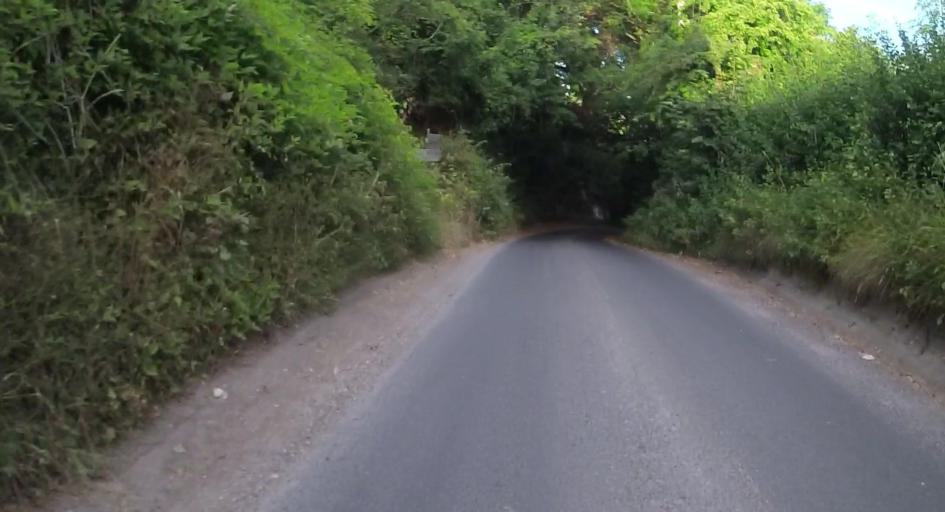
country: GB
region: England
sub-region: Dorset
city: Wareham
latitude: 50.6379
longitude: -2.0960
